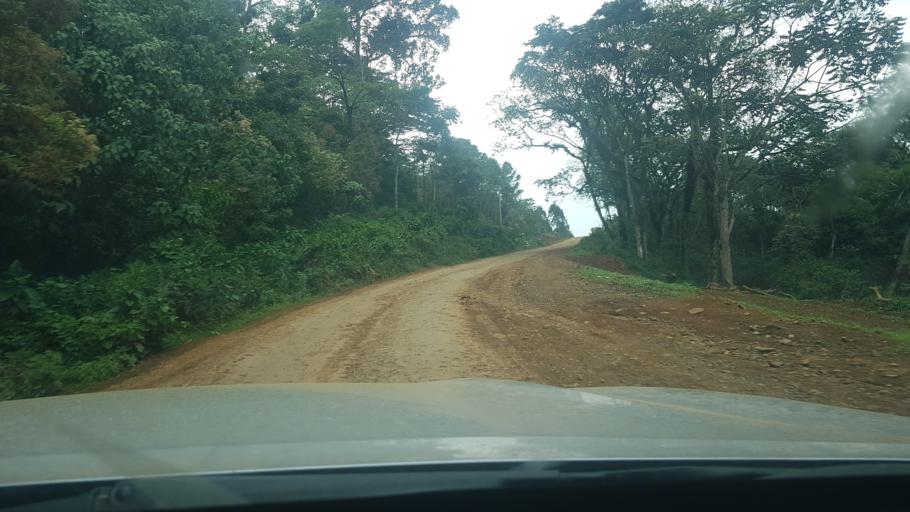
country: ET
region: Oromiya
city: Gore
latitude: 7.9081
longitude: 35.5068
